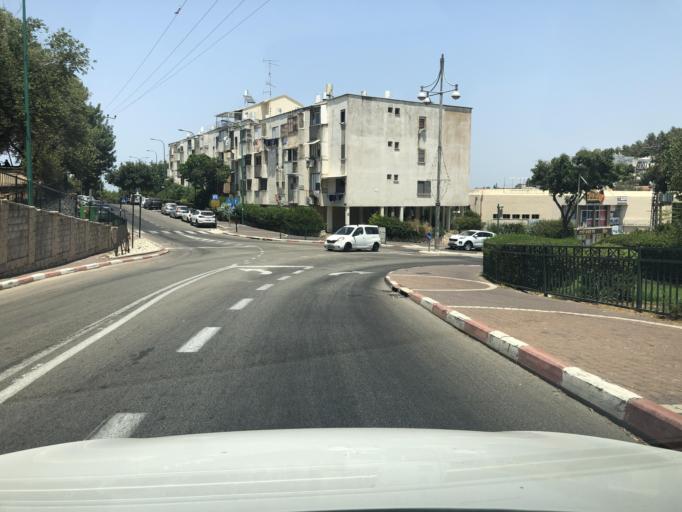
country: IL
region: Haifa
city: Daliyat el Karmil
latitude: 32.6544
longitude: 35.1034
